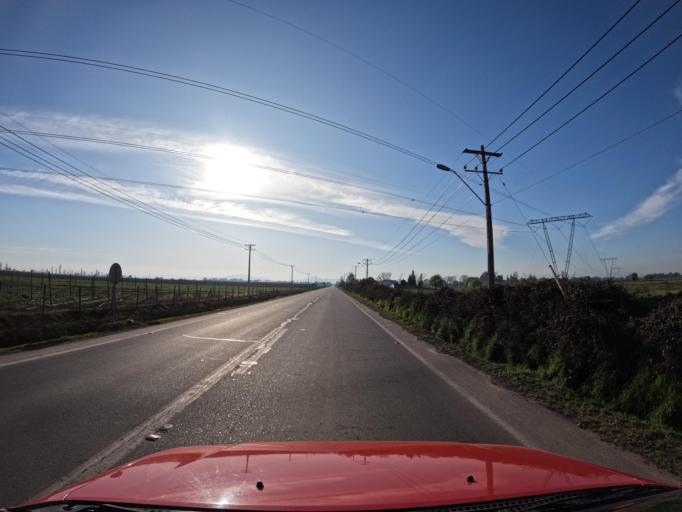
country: CL
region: Maule
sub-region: Provincia de Curico
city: Teno
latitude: -34.8985
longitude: -71.0581
